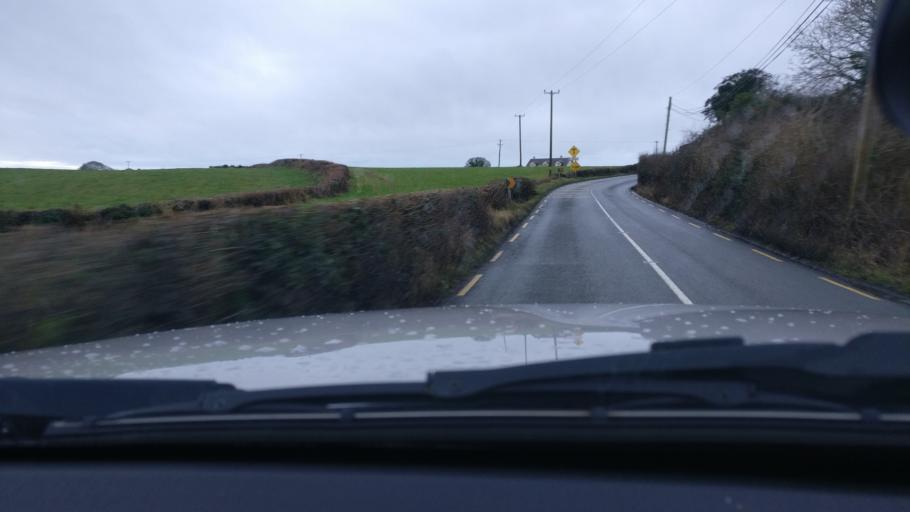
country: IE
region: Leinster
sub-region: An Longfort
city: Granard
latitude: 53.7937
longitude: -7.3942
